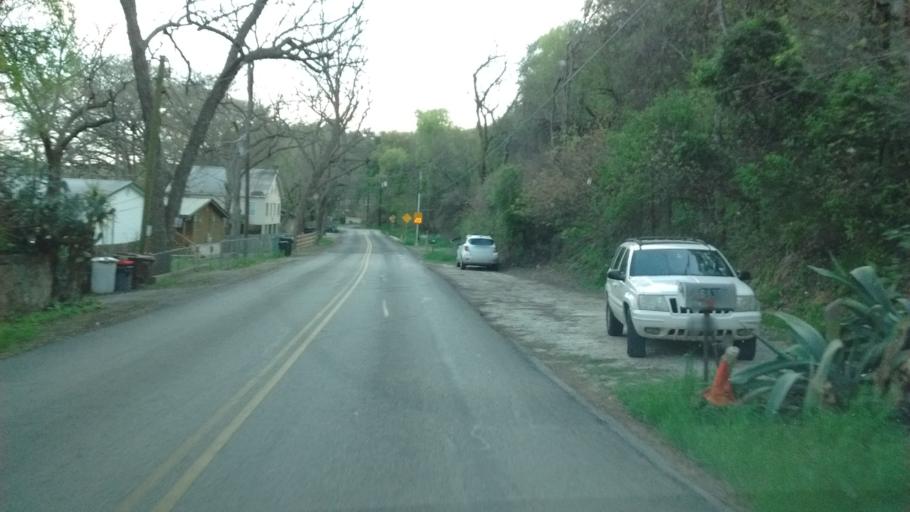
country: US
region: Texas
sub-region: Comal County
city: New Braunfels
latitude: 29.7811
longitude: -98.1597
